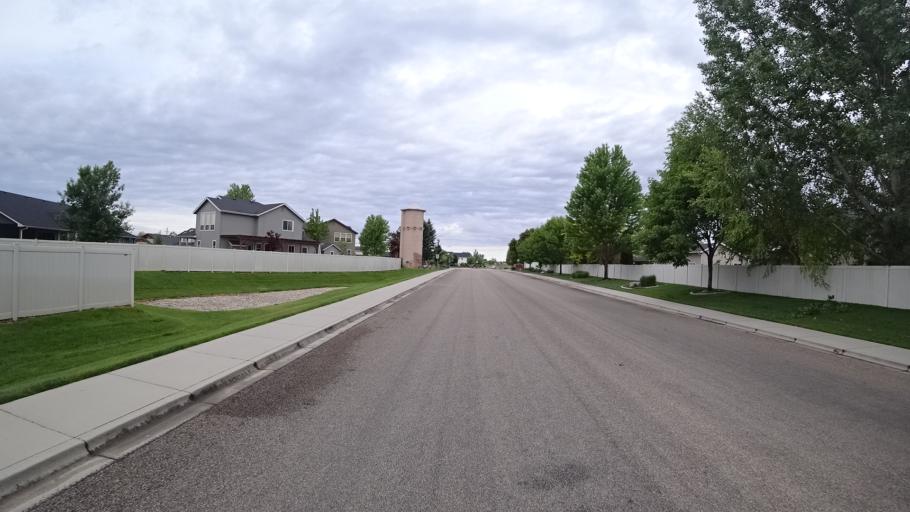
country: US
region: Idaho
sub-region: Ada County
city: Star
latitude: 43.7012
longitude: -116.4918
